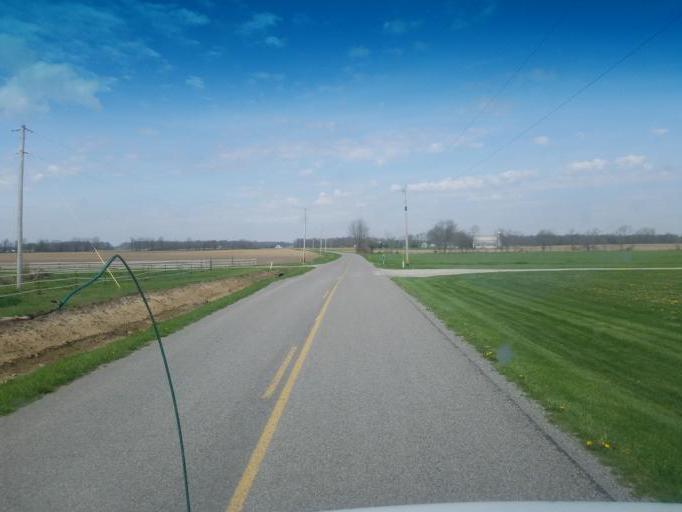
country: US
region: Ohio
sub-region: Logan County
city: Northwood
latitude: 40.4945
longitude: -83.6088
